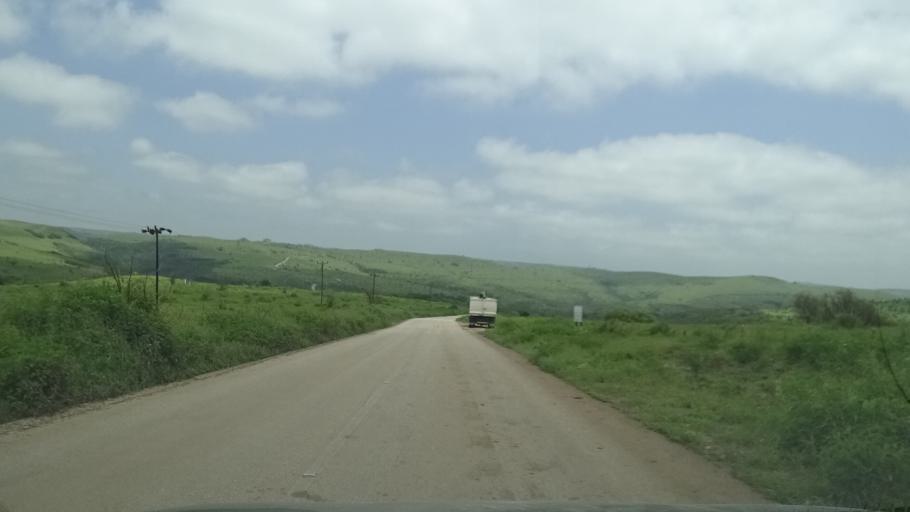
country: OM
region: Zufar
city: Salalah
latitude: 17.1950
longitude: 54.1709
